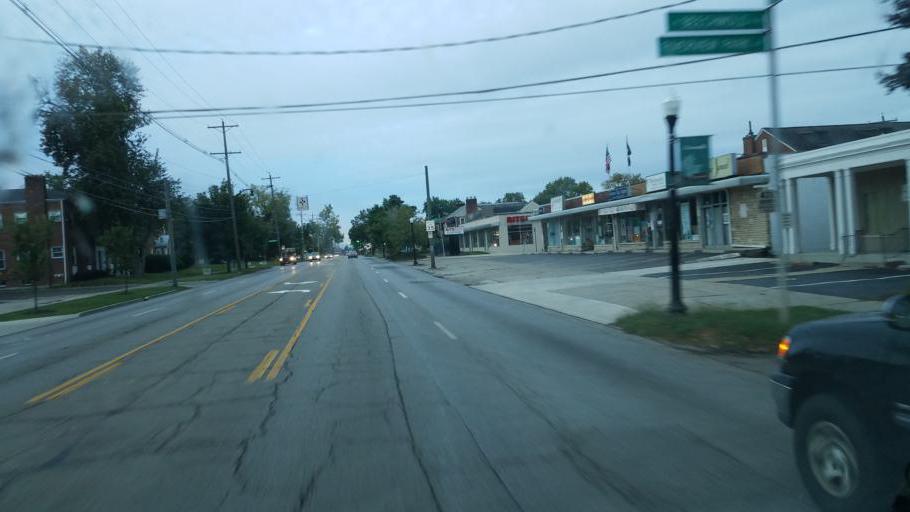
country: US
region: Ohio
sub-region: Franklin County
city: Worthington
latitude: 40.0586
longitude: -83.0198
